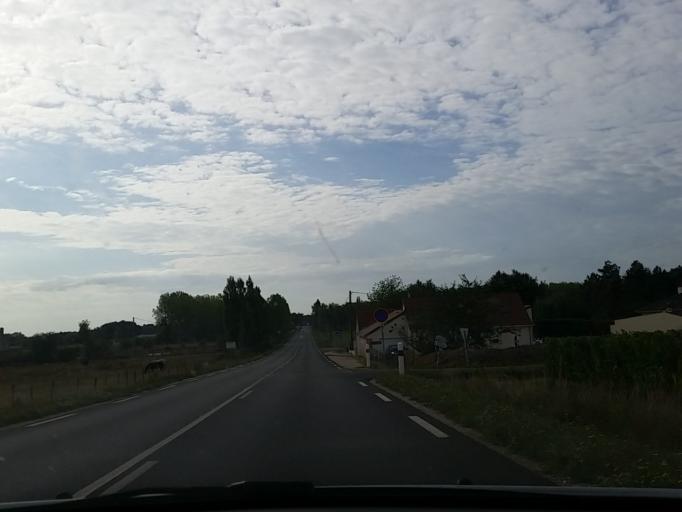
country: FR
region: Centre
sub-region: Departement du Loir-et-Cher
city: Cheverny
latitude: 47.4870
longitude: 1.4860
